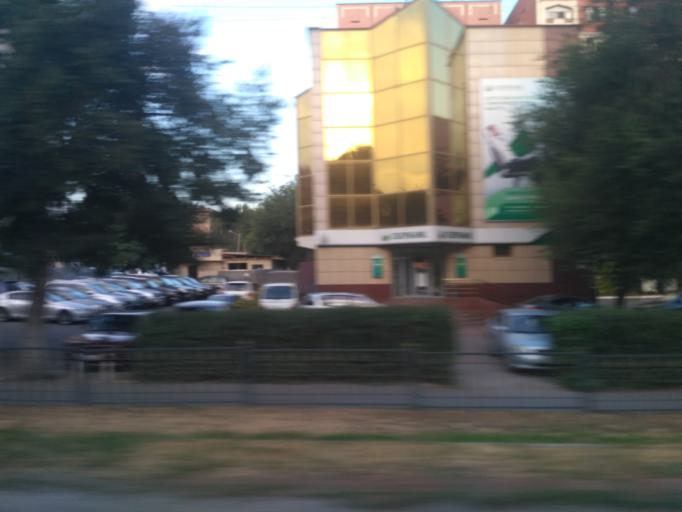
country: KZ
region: Almaty Qalasy
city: Almaty
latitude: 43.2603
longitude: 76.8869
